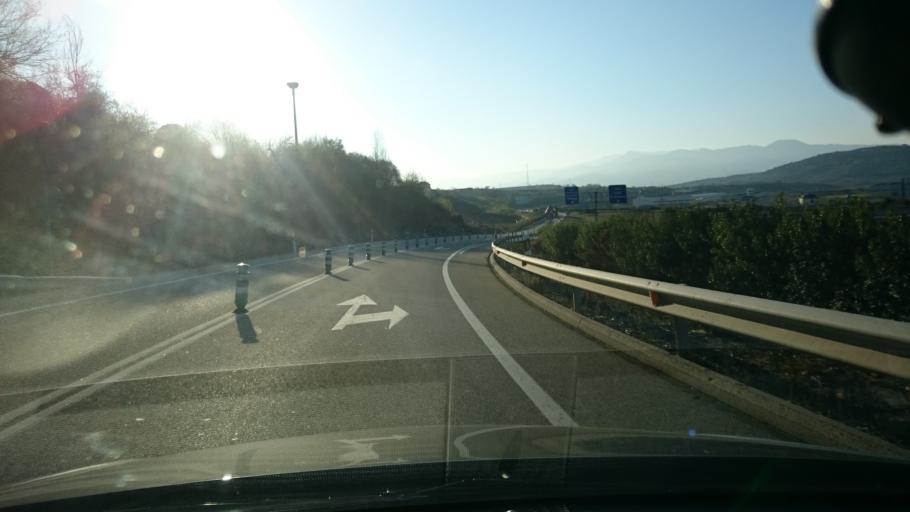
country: ES
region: Castille and Leon
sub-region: Provincia de Leon
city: Villafranca del Bierzo
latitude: 42.5982
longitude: -6.8045
